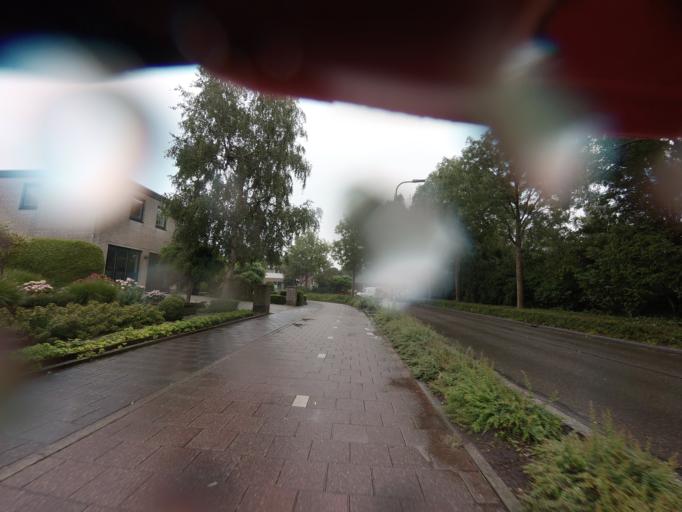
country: NL
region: North Holland
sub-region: Gemeente Medemblik
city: Medemblik
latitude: 52.7661
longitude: 5.1110
